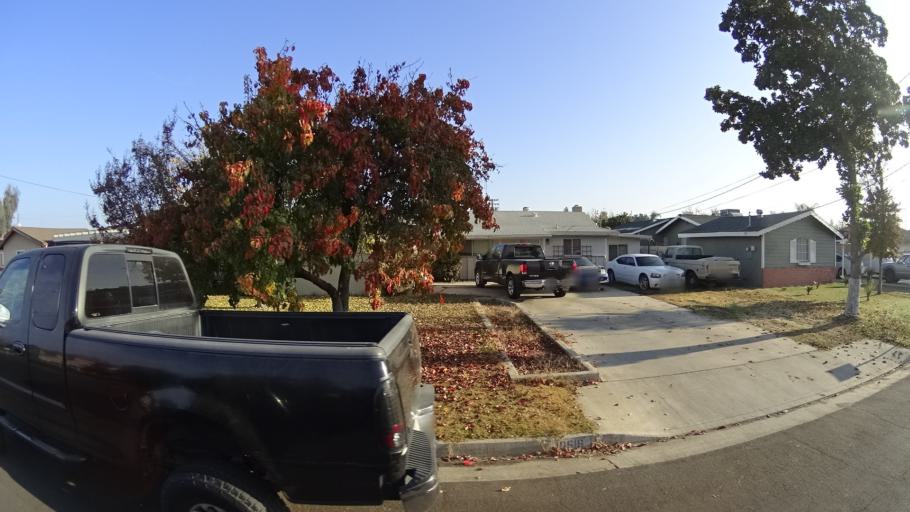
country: US
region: California
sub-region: Kern County
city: Greenacres
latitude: 35.3818
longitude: -119.1209
